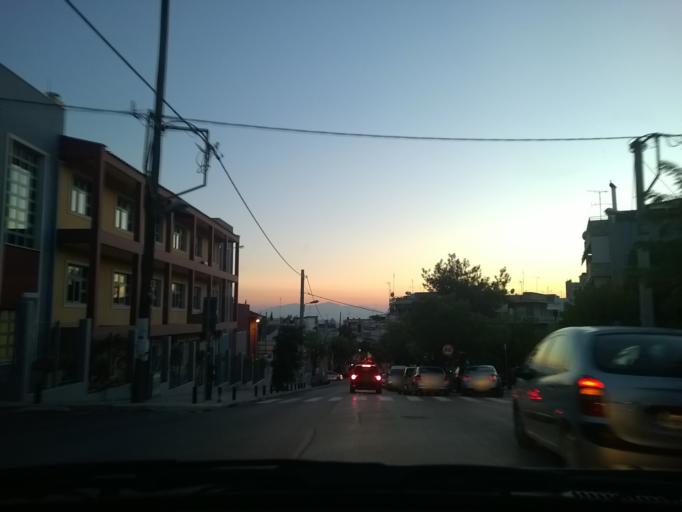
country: GR
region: Central Macedonia
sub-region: Nomos Thessalonikis
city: Polichni
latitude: 40.6637
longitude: 22.9483
